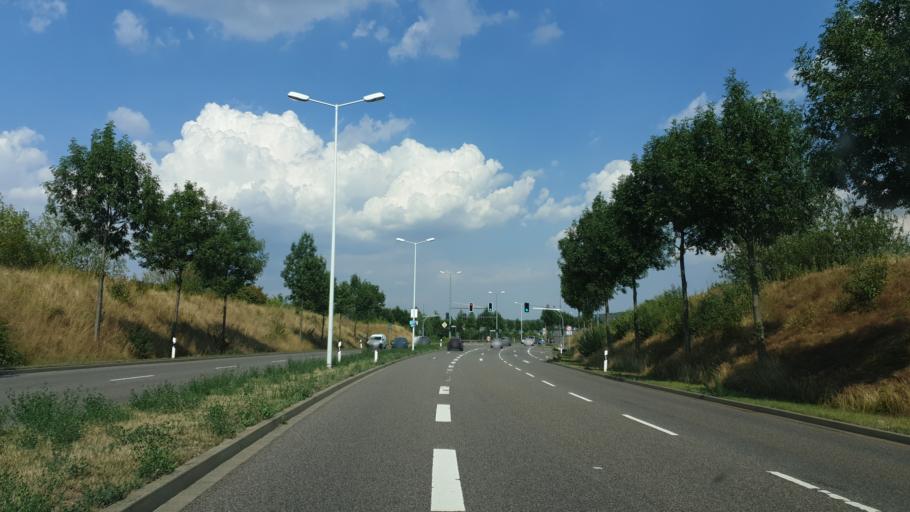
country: DE
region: Saxony
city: Hilbersdorf
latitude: 50.8176
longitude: 12.9643
